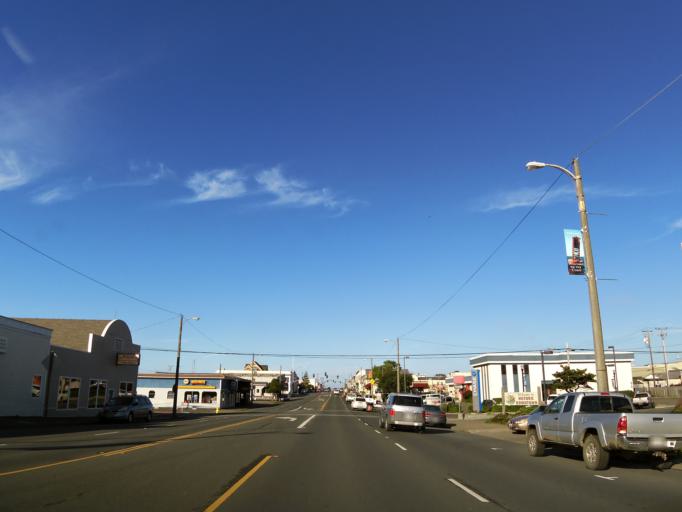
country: US
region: California
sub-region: Mendocino County
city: Fort Bragg
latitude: 39.4424
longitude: -123.8060
